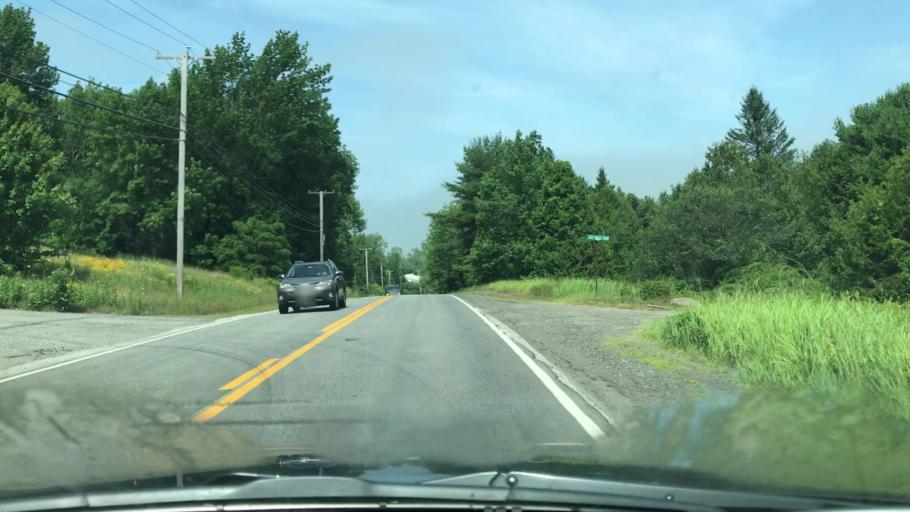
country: US
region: Maine
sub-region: Waldo County
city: Lincolnville
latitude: 44.2683
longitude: -69.0167
